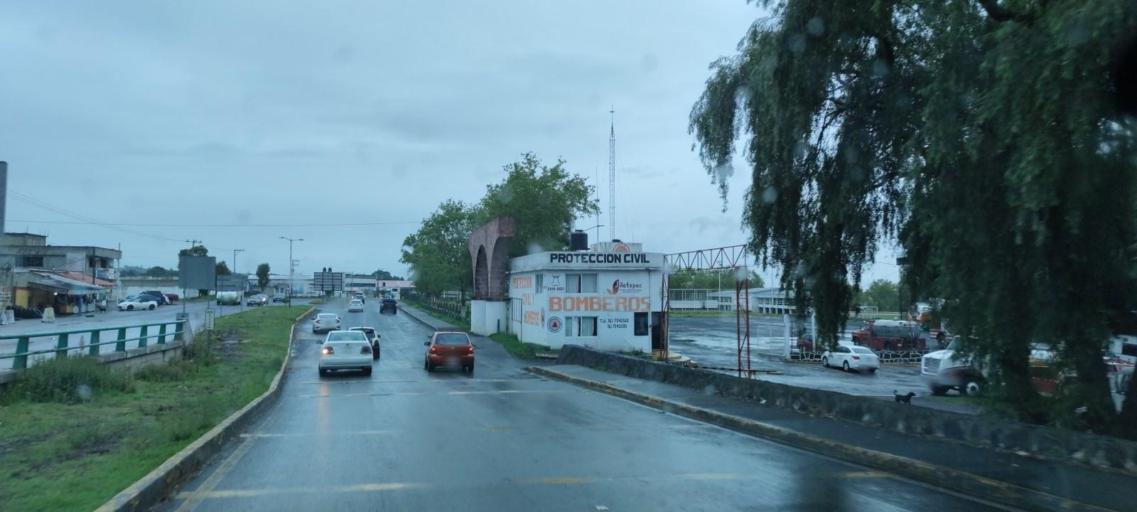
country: MX
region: Mexico
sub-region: Jilotepec
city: Xhixhata
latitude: 19.9555
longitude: -99.5483
